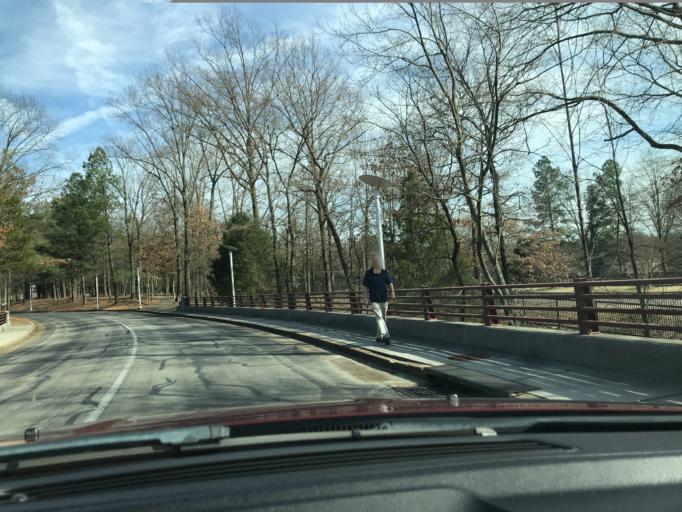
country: US
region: Tennessee
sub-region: Shelby County
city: Germantown
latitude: 35.0487
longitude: -89.7931
